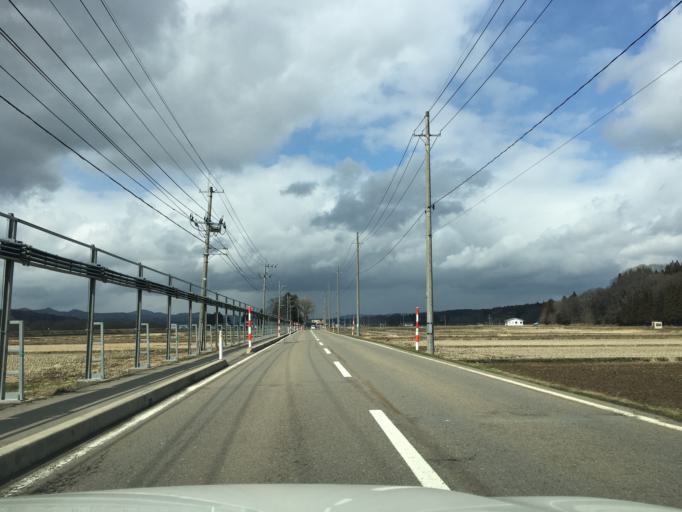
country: JP
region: Akita
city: Takanosu
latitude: 40.1314
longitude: 140.3591
